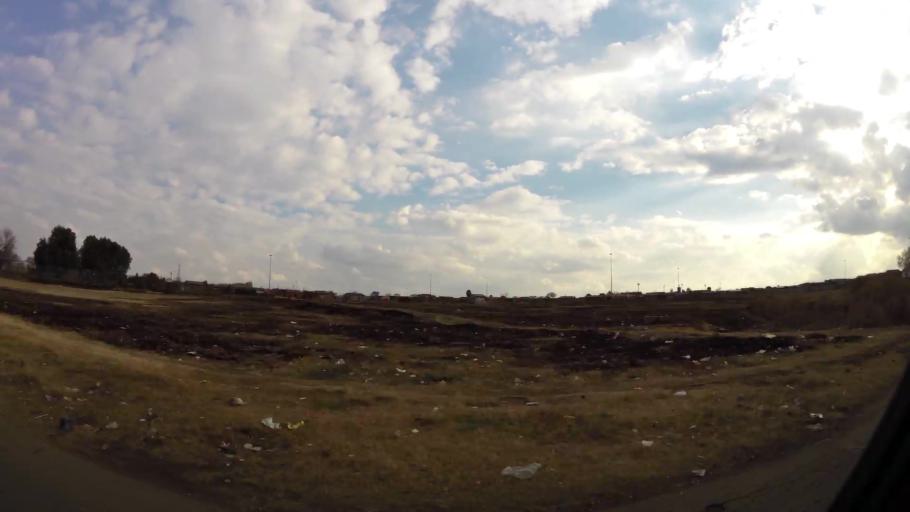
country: ZA
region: Gauteng
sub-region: Sedibeng District Municipality
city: Vereeniging
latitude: -26.6871
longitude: 27.8802
